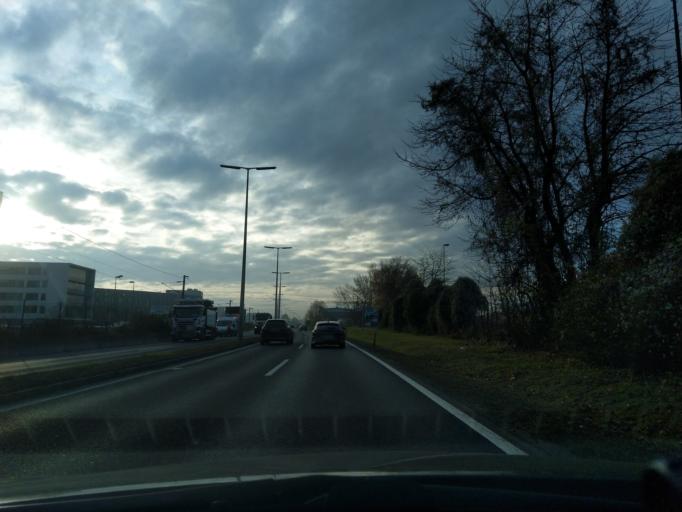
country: AT
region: Upper Austria
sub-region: Linz Stadt
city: Linz
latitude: 48.2805
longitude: 14.3174
